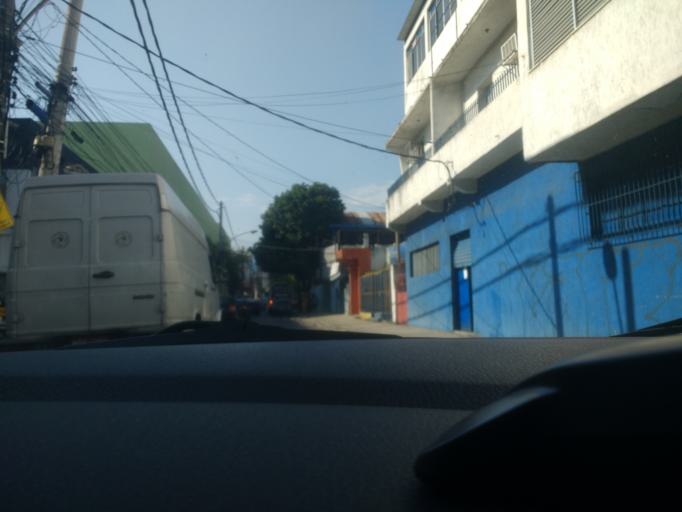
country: BR
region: Rio de Janeiro
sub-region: Duque De Caxias
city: Duque de Caxias
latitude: -22.7933
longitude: -43.3015
